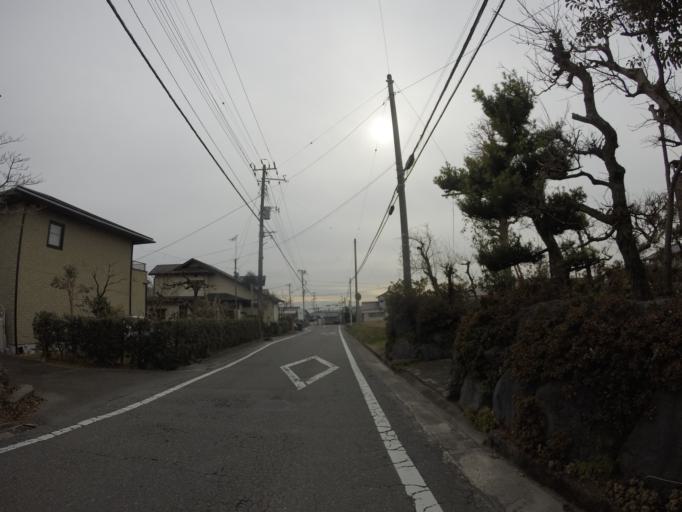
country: JP
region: Shizuoka
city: Fujinomiya
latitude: 35.2425
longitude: 138.6289
